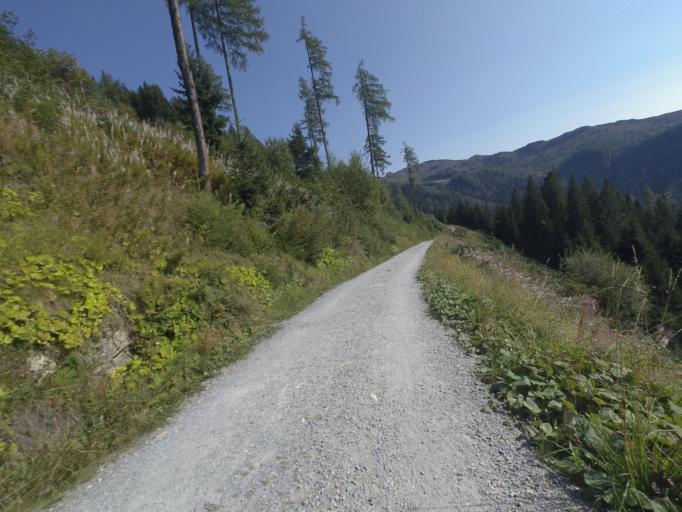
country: AT
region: Salzburg
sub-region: Politischer Bezirk Sankt Johann im Pongau
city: Kleinarl
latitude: 47.2749
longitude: 13.2575
